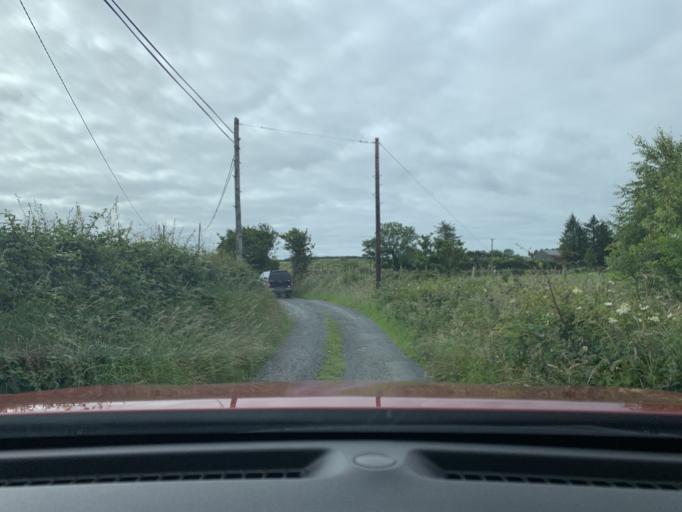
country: IE
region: Connaught
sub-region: Sligo
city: Sligo
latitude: 54.3780
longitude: -8.5206
